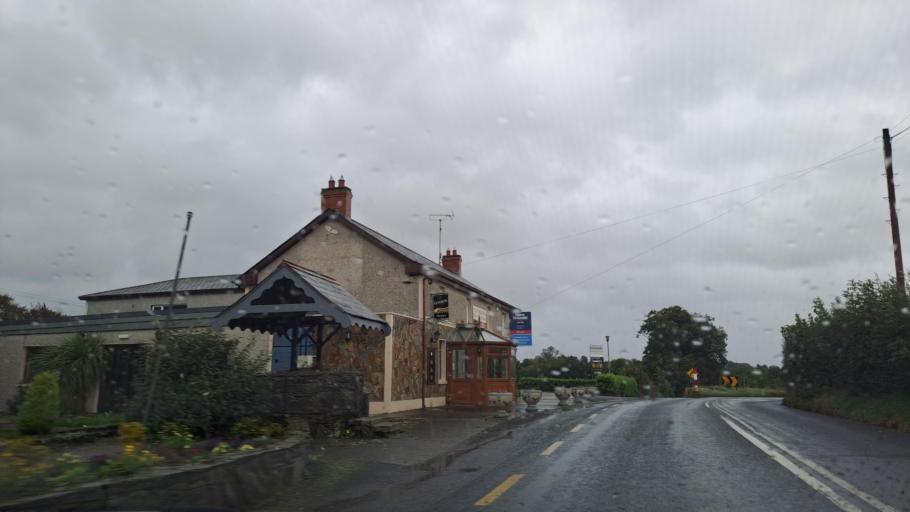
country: IE
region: Leinster
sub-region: Lu
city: Dundalk
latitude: 53.9786
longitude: -6.5229
